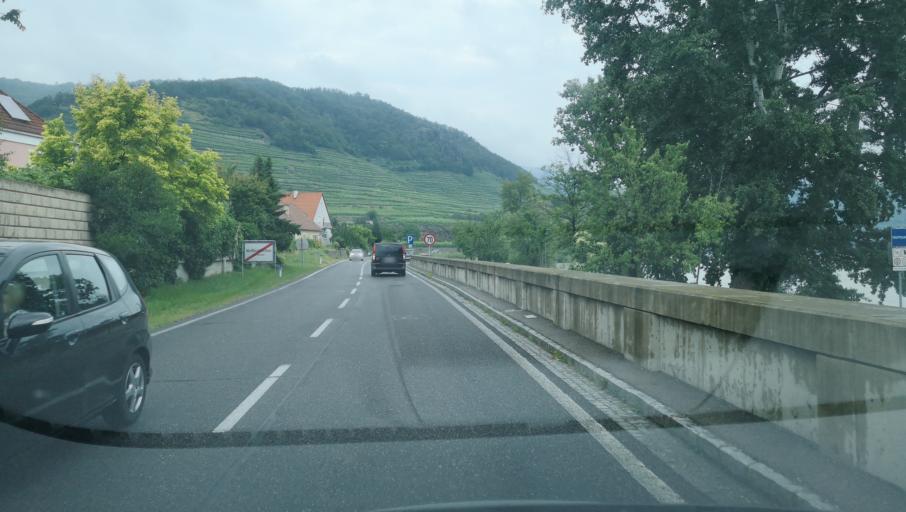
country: AT
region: Lower Austria
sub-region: Politischer Bezirk Krems
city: Weinzierl am Walde
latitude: 48.3969
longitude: 15.4737
